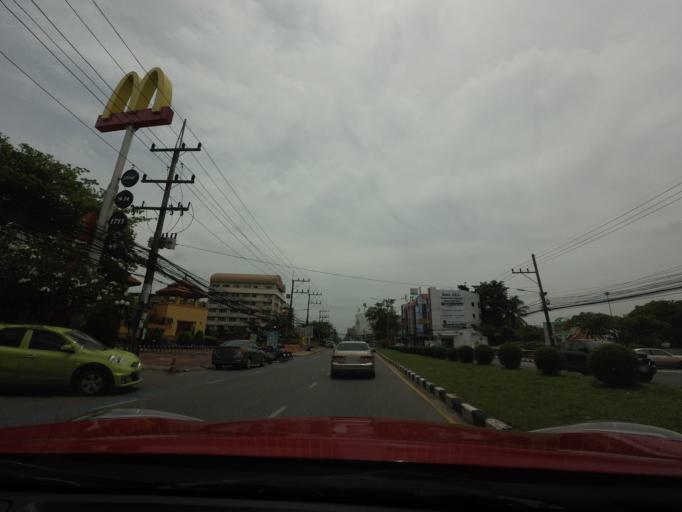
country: TH
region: Songkhla
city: Hat Yai
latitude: 6.9983
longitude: 100.4775
